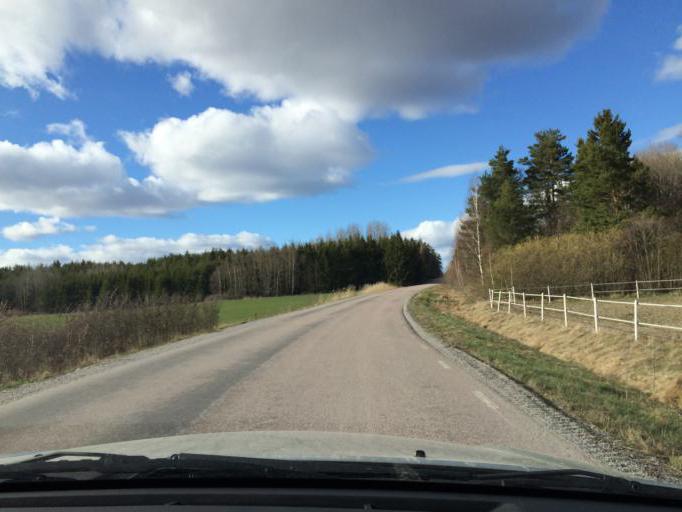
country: SE
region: Soedermanland
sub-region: Eskilstuna Kommun
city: Hallbybrunn
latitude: 59.4183
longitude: 16.4364
